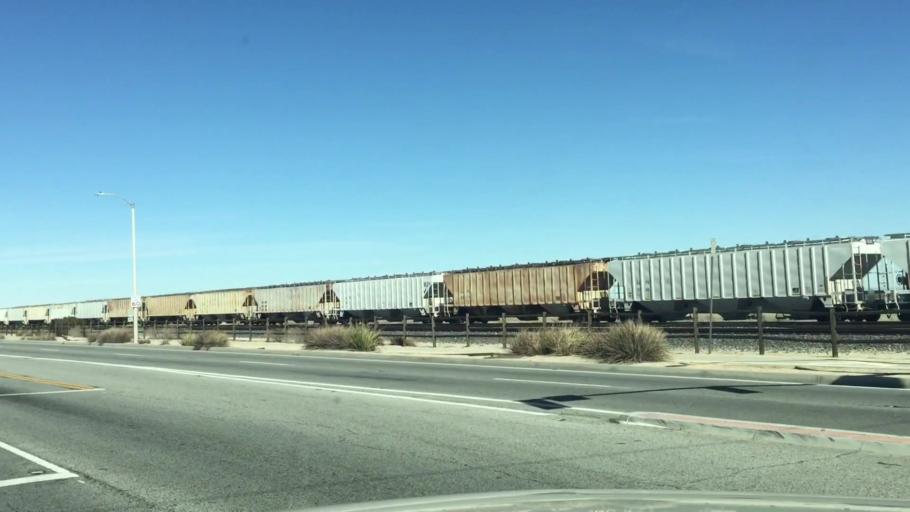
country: US
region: California
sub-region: Los Angeles County
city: Desert View Highlands
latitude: 34.6313
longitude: -118.1260
